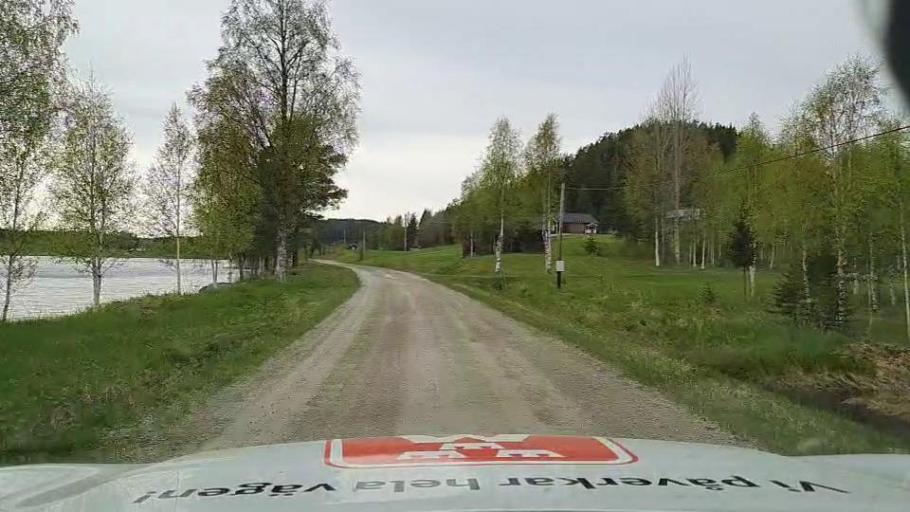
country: SE
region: Jaemtland
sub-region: Bergs Kommun
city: Hoverberg
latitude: 62.6836
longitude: 14.7957
